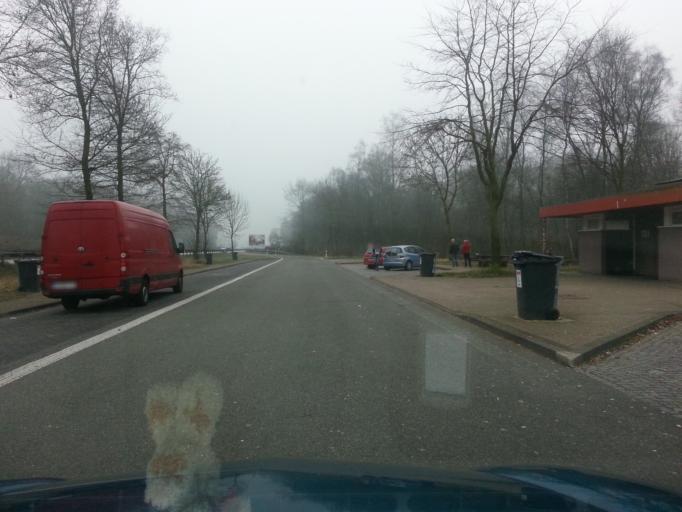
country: DE
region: North Rhine-Westphalia
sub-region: Regierungsbezirk Dusseldorf
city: Emmerich
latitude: 51.8740
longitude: 6.1953
